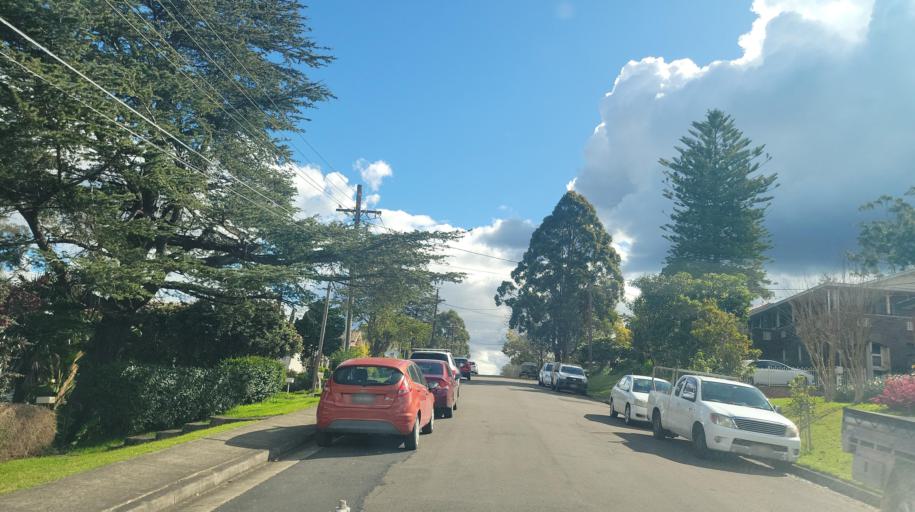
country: AU
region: New South Wales
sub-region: Hornsby Shire
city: Pennant Hills
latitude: -33.7370
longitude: 151.0774
